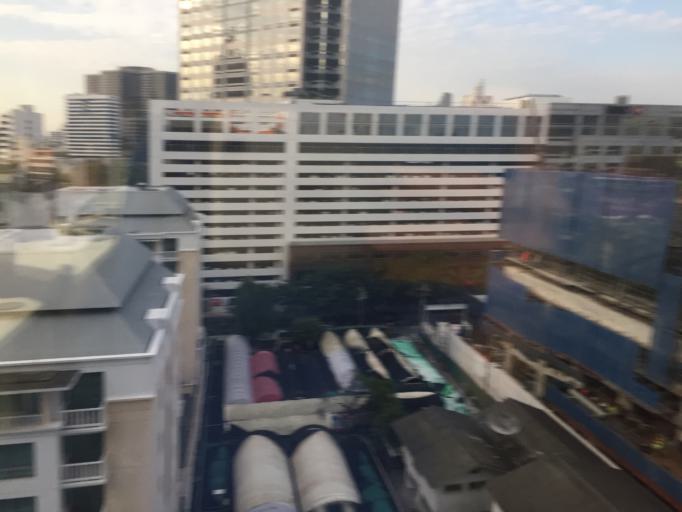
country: TH
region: Bangkok
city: Bang Rak
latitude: 13.7258
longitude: 100.5409
